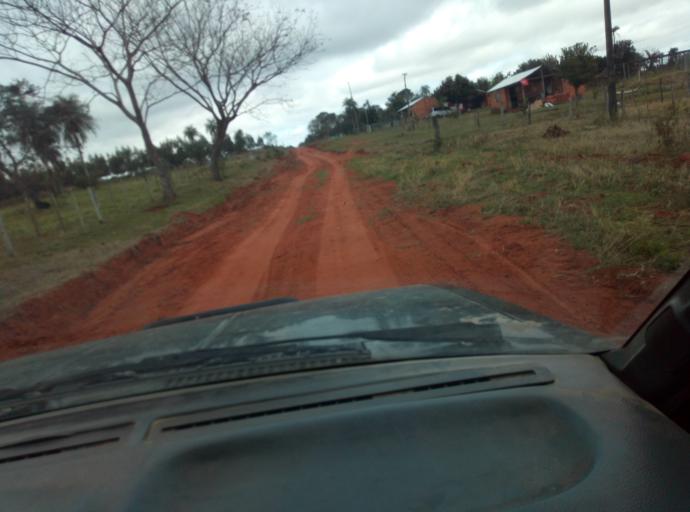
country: PY
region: Caaguazu
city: Doctor Cecilio Baez
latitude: -25.1464
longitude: -56.2903
